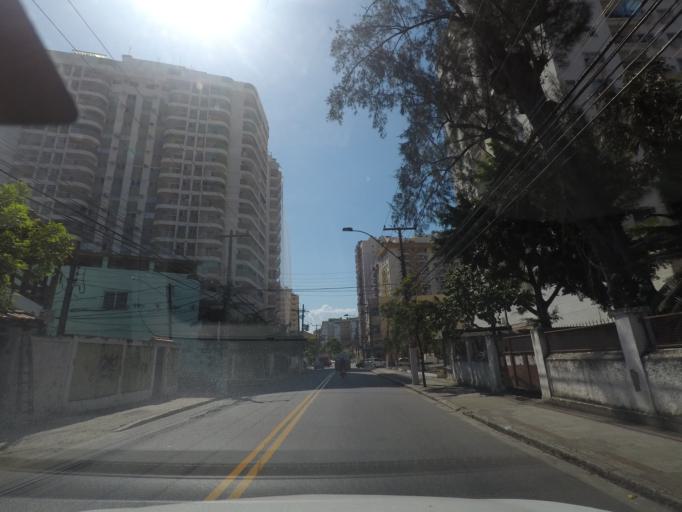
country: BR
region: Rio de Janeiro
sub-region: Niteroi
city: Niteroi
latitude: -22.9046
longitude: -43.0922
